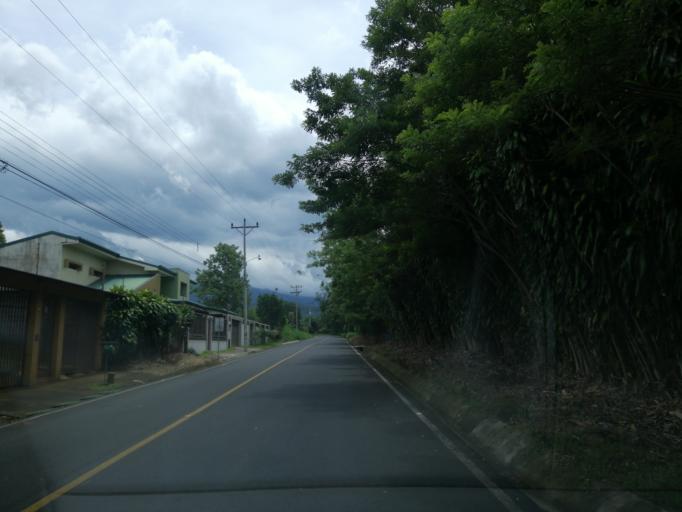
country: CR
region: Alajuela
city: Alajuela
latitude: 10.0297
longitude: -84.1954
